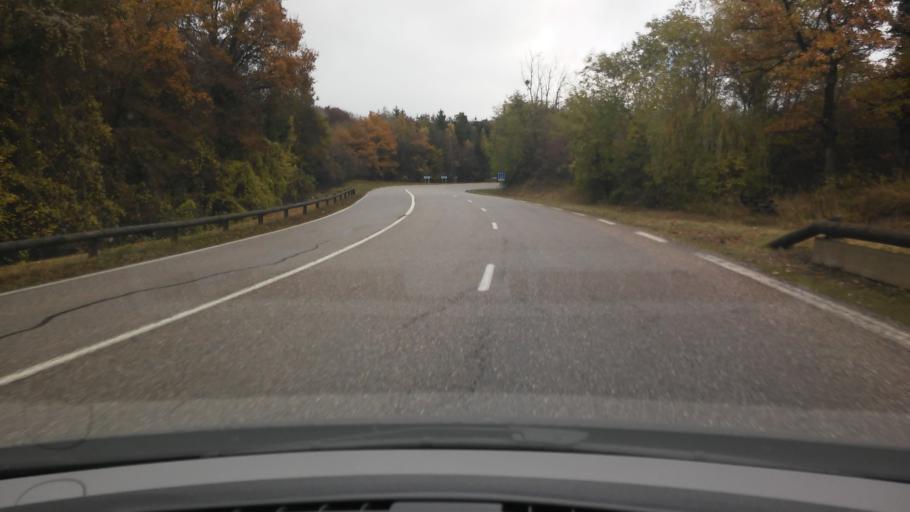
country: FR
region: Lorraine
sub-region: Departement de la Moselle
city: Kedange-sur-Canner
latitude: 49.2984
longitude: 6.3644
